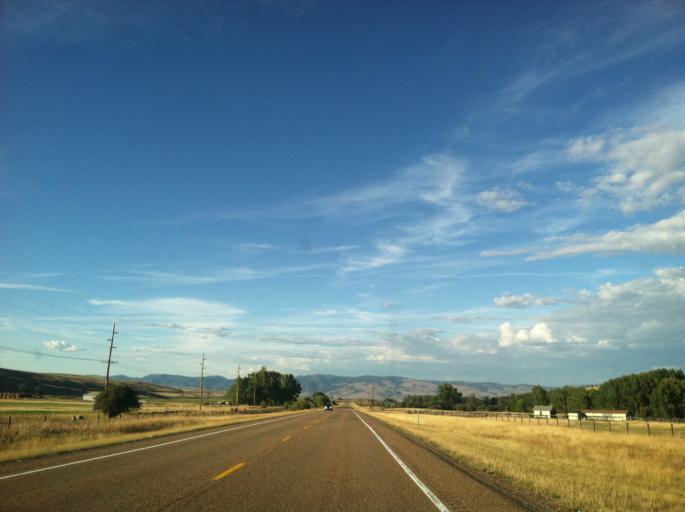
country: US
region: Montana
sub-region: Granite County
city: Philipsburg
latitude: 46.5358
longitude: -113.2220
